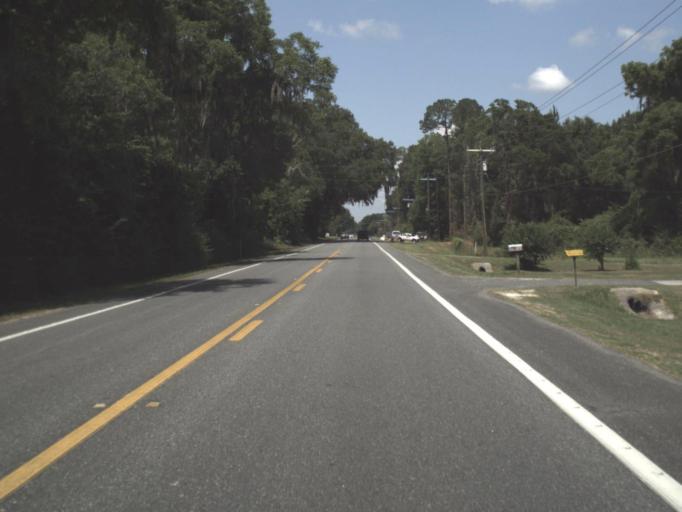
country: US
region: Florida
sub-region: Levy County
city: Williston
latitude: 29.3744
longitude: -82.4656
